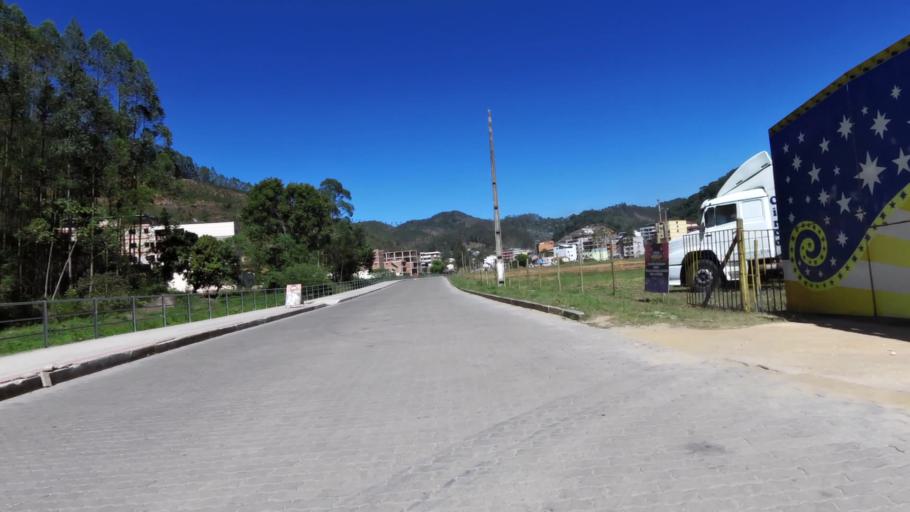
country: BR
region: Espirito Santo
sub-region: Vargem Alta
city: Vargem Alta
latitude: -20.6708
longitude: -41.0054
